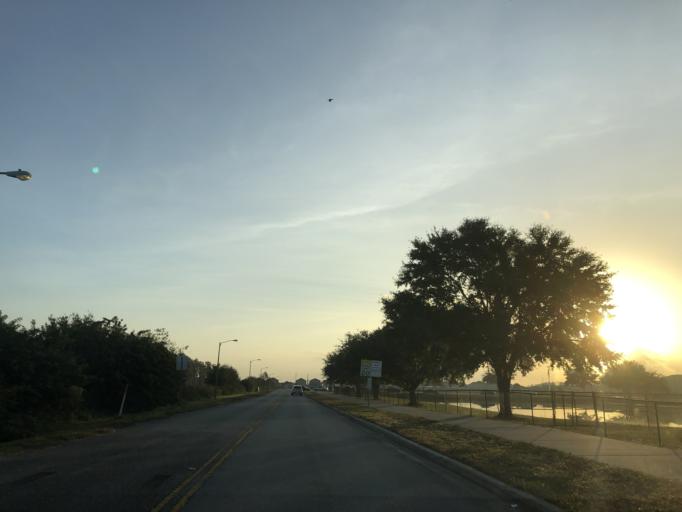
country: US
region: Florida
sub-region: Osceola County
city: Kissimmee
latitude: 28.3191
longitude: -81.4414
